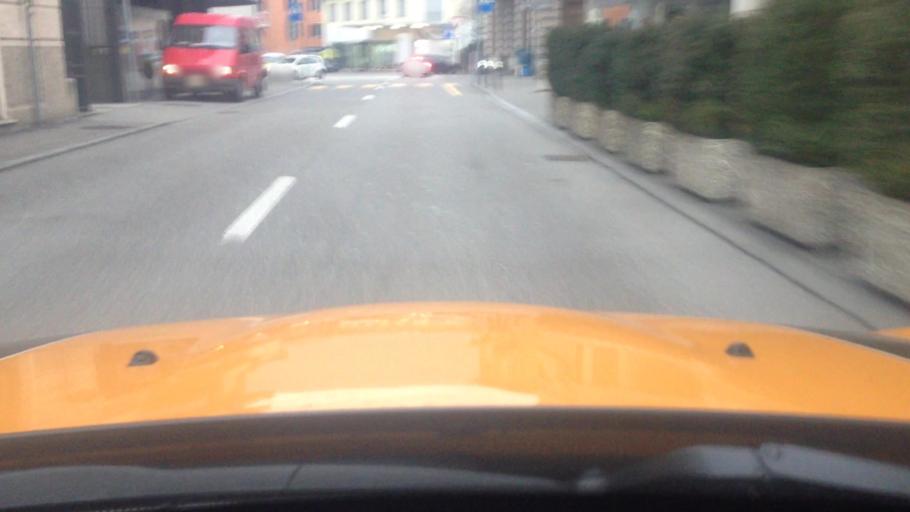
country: CH
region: Ticino
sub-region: Mendrisio District
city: Chiasso
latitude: 45.8352
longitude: 9.0314
